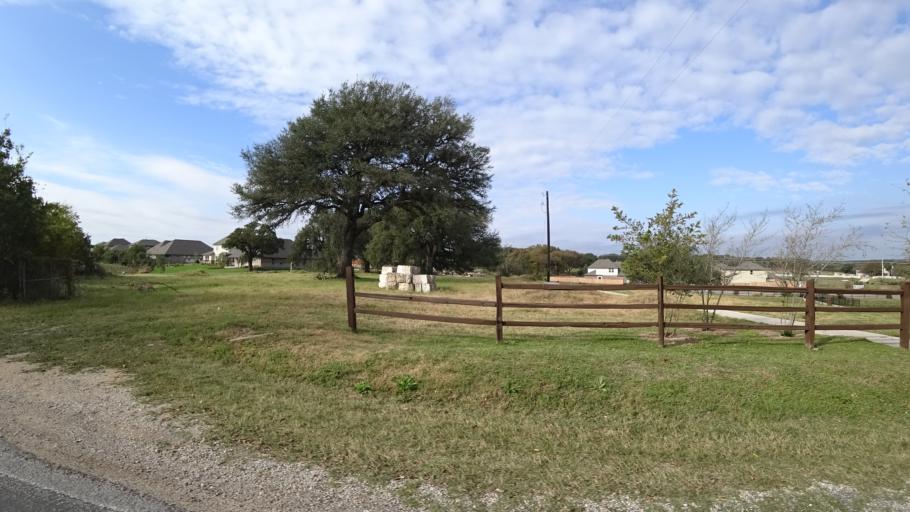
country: US
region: Texas
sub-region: Travis County
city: Manchaca
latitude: 30.1368
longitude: -97.8466
